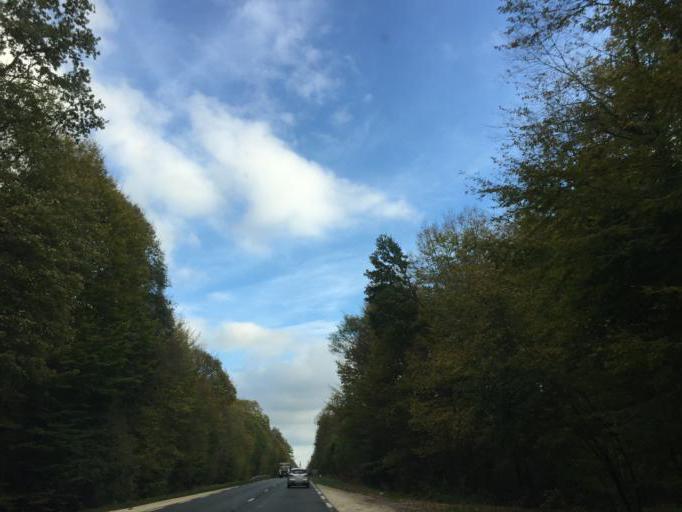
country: FR
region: Ile-de-France
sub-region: Departement de Seine-et-Marne
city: Villeneuve-le-Comte
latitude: 48.7951
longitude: 2.8626
